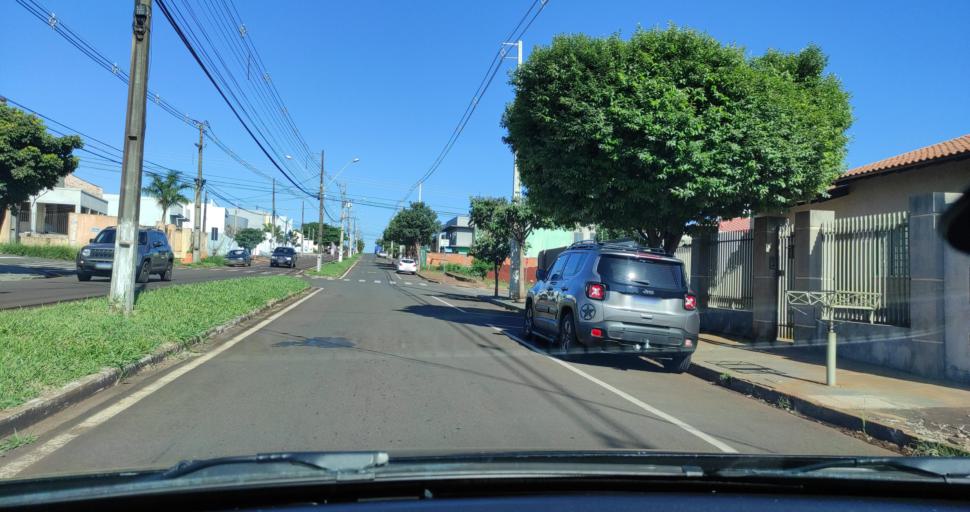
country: BR
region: Parana
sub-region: Ibipora
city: Ibipora
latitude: -23.2743
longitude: -51.0666
